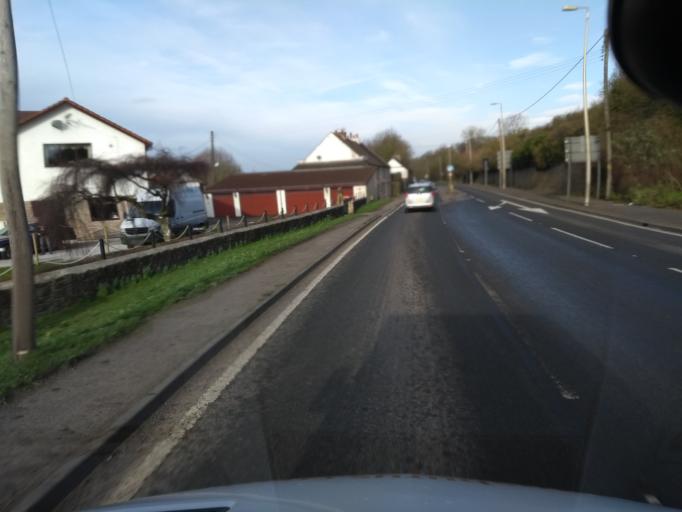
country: GB
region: England
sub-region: North Somerset
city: Bleadon
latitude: 51.3087
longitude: -2.9600
